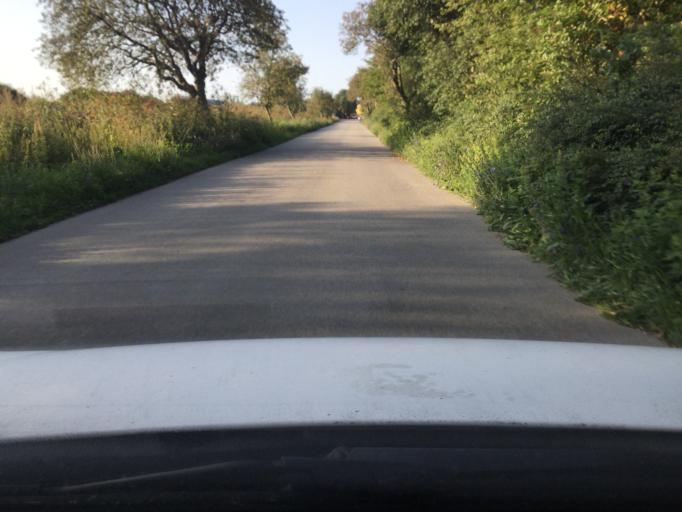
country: DK
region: Zealand
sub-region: Lolland Kommune
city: Rodby
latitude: 54.7001
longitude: 11.3881
